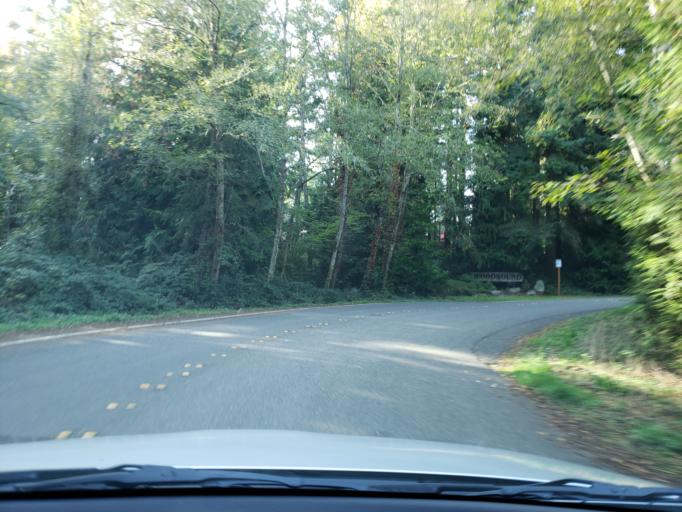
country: US
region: Washington
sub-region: Snohomish County
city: Meadowdale
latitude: 47.8681
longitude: -122.3171
